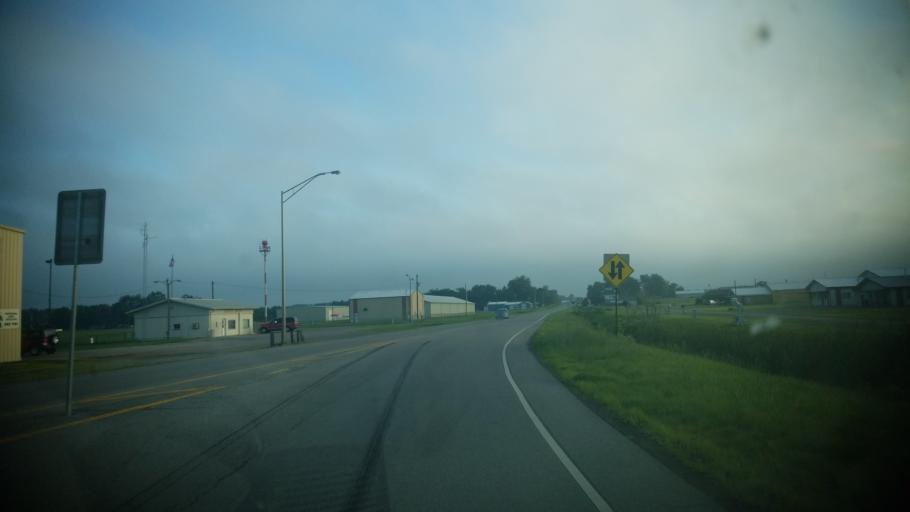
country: US
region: Illinois
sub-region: Wayne County
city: Fairfield
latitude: 38.3802
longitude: -88.4057
